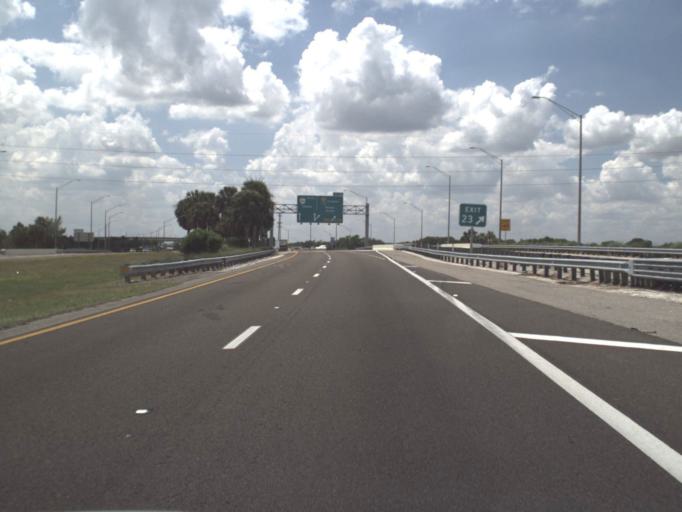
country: US
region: Florida
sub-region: Orange County
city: Ocoee
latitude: 28.5601
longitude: -81.5598
